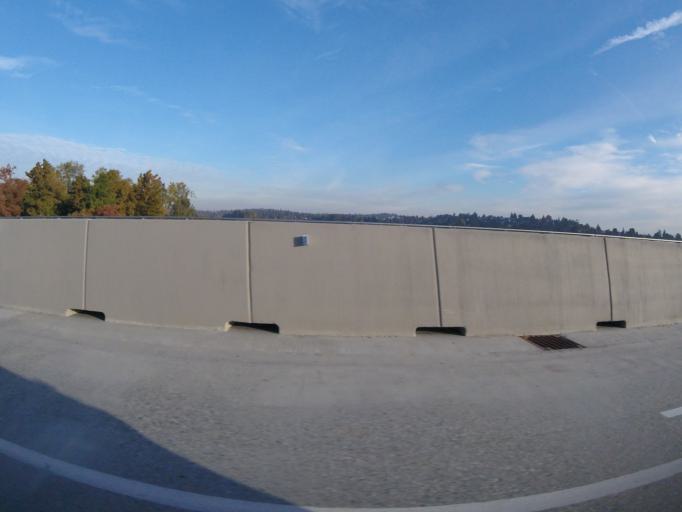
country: US
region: Washington
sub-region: King County
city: Seattle
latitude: 47.6451
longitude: -122.2890
